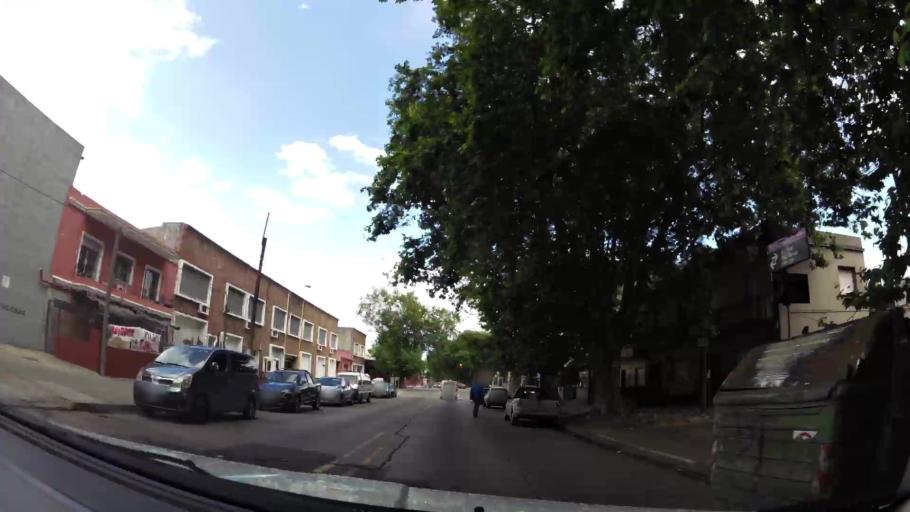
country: UY
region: Montevideo
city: Montevideo
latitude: -34.8652
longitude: -56.1800
